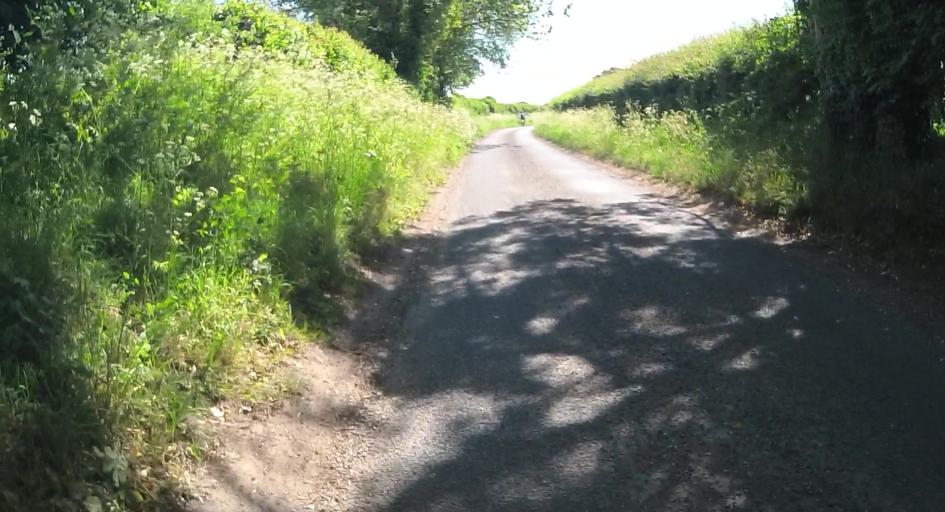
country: GB
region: England
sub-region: Hampshire
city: Old Basing
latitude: 51.2509
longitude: -1.0241
